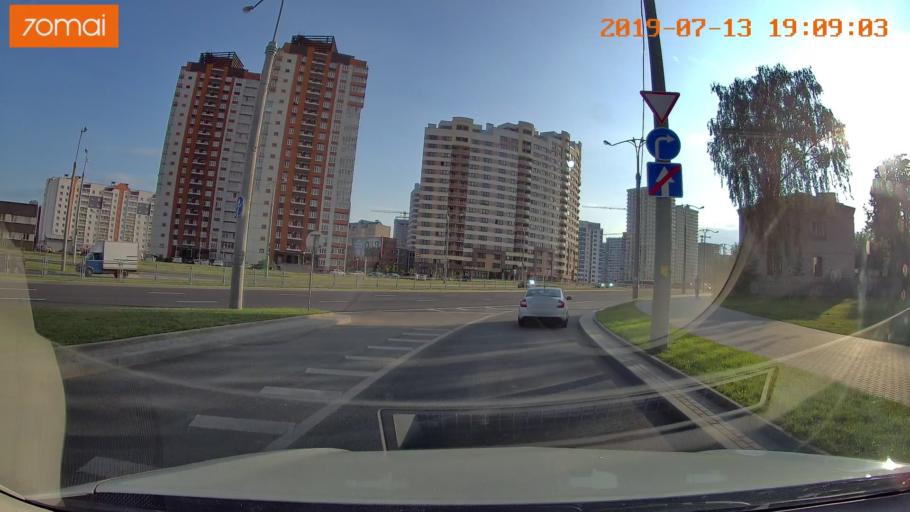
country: BY
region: Minsk
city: Minsk
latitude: 53.8728
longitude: 27.5594
